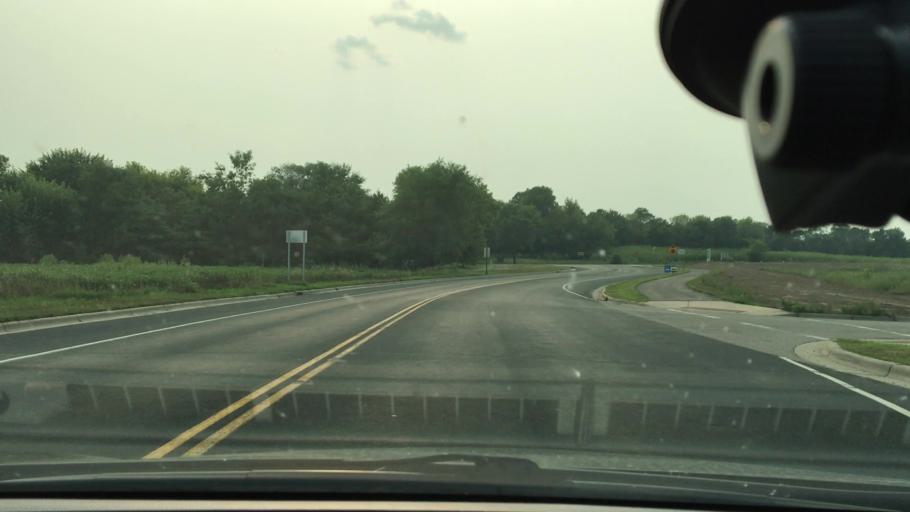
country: US
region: Minnesota
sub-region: Wright County
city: Otsego
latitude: 45.2595
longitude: -93.5895
